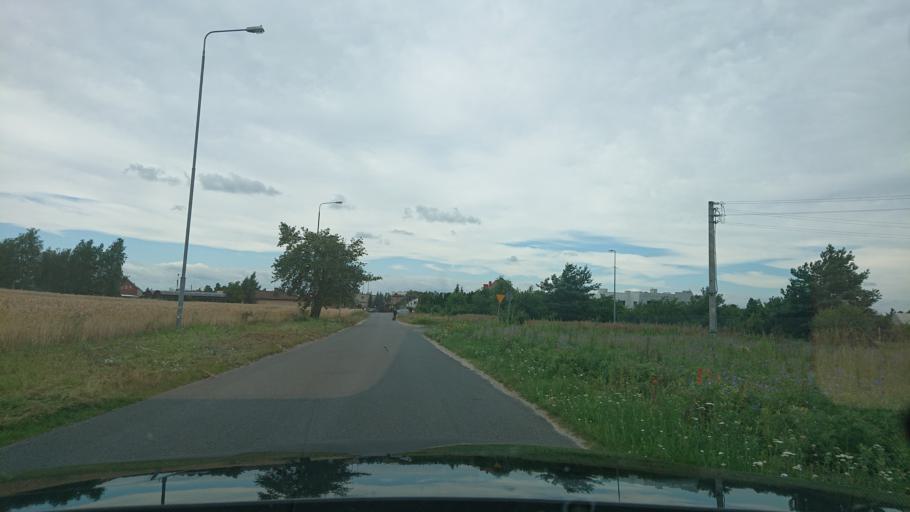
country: PL
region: Greater Poland Voivodeship
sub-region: Powiat gnieznienski
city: Gniezno
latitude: 52.5101
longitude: 17.6064
